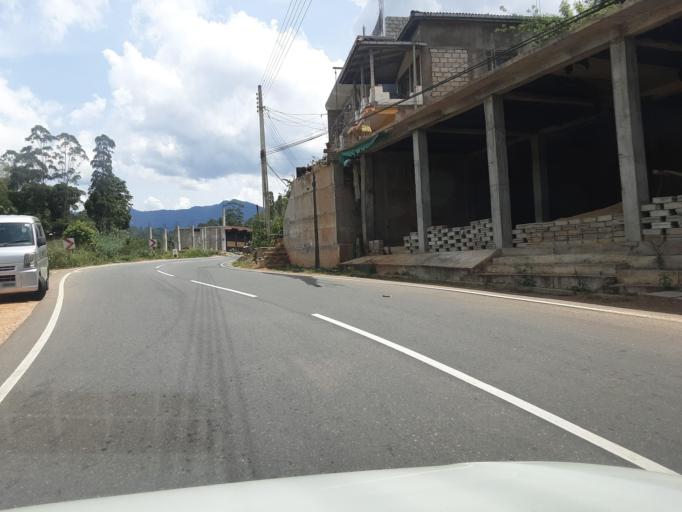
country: LK
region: Central
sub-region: Nuwara Eliya District
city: Nuwara Eliya
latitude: 6.9206
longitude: 80.9010
